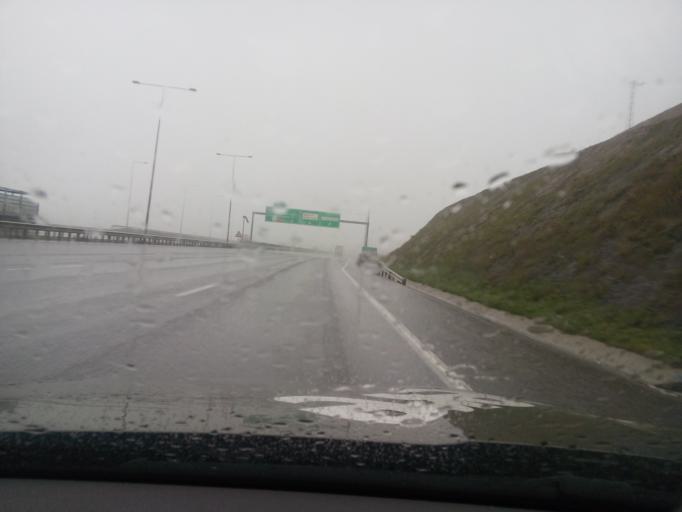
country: TR
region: Istanbul
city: Basaksehir
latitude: 41.1460
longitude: 28.8065
